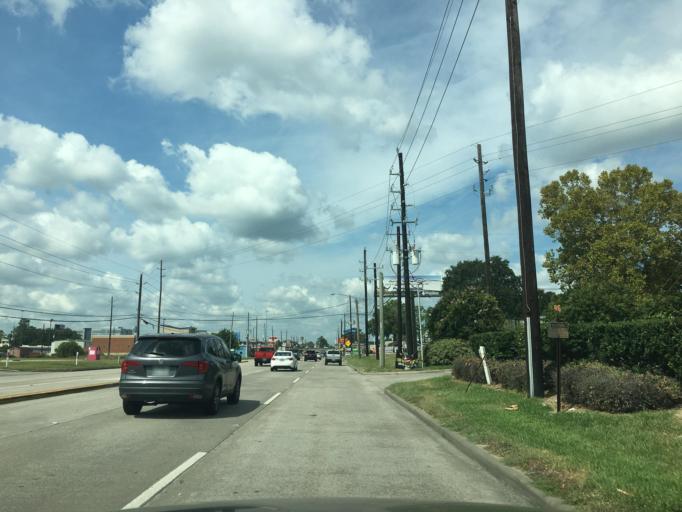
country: US
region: Texas
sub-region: Montgomery County
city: Oak Ridge North
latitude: 30.1274
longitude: -95.4362
